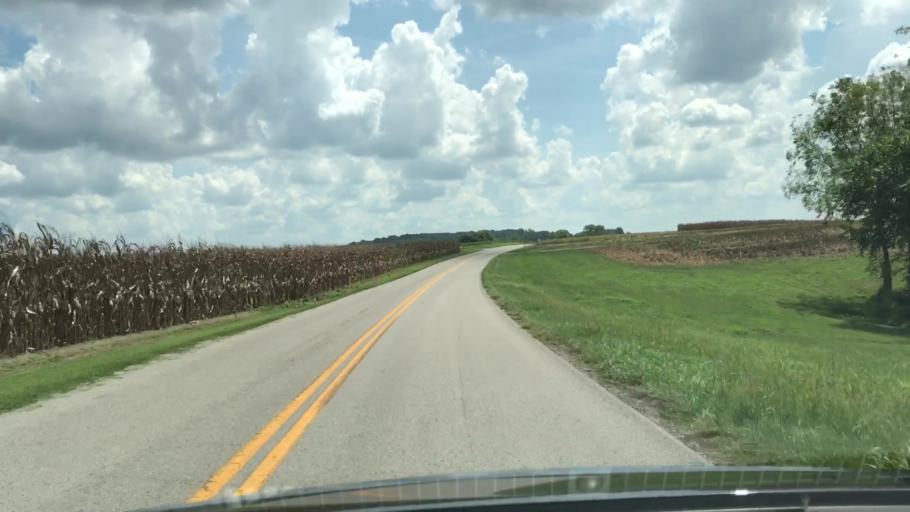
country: US
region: Kentucky
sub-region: Todd County
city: Guthrie
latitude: 36.7089
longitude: -87.0491
